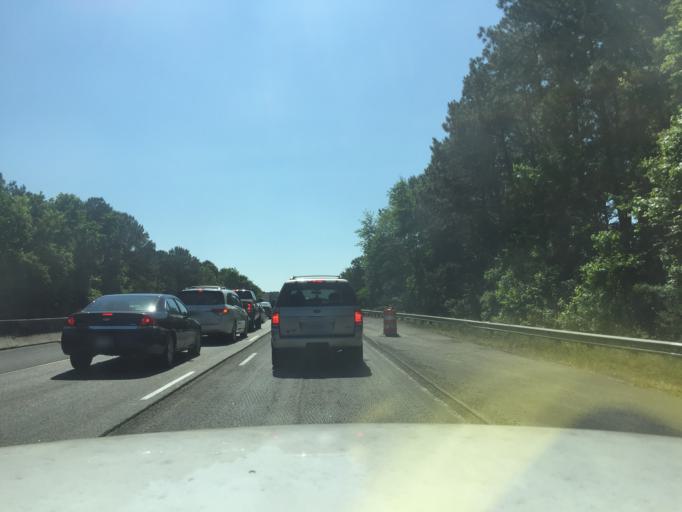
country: US
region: Georgia
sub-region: Chatham County
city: Georgetown
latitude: 31.9938
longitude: -81.2333
